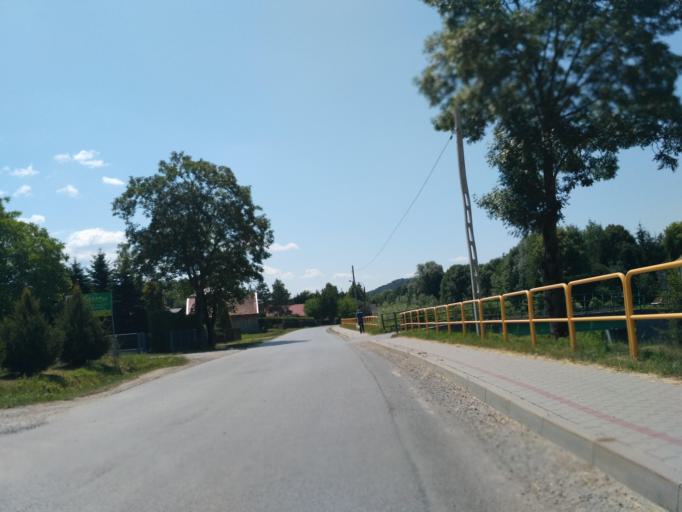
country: PL
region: Subcarpathian Voivodeship
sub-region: Powiat sanocki
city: Niebieszczany
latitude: 49.5267
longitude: 22.1277
